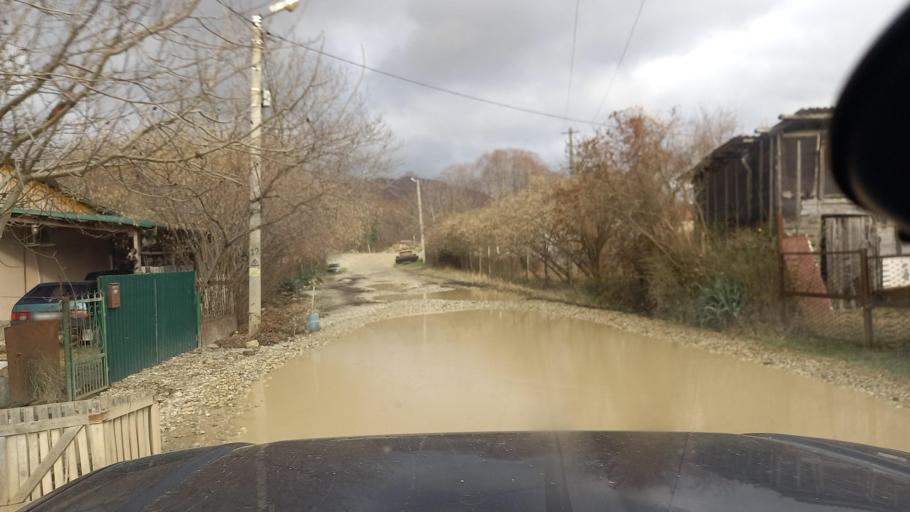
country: RU
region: Krasnodarskiy
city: Pshada
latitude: 44.4804
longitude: 38.4021
